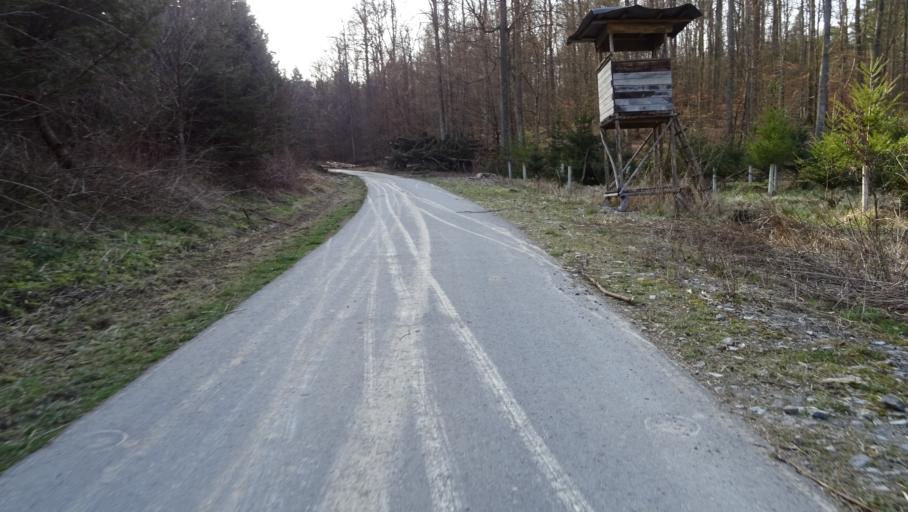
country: DE
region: Baden-Wuerttemberg
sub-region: Regierungsbezirk Stuttgart
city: Roigheim
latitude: 49.3910
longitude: 9.3300
